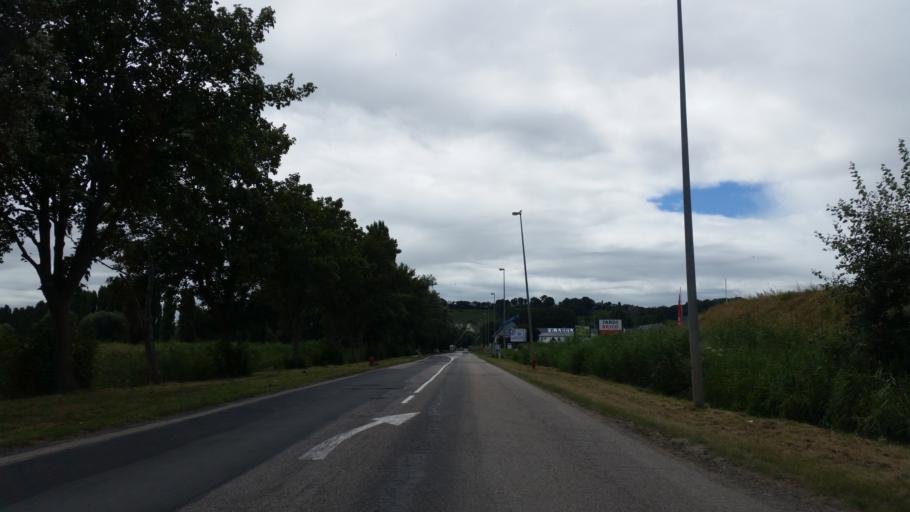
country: FR
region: Lower Normandy
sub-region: Departement du Calvados
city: La Riviere-Saint-Sauveur
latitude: 49.4182
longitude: 0.2597
